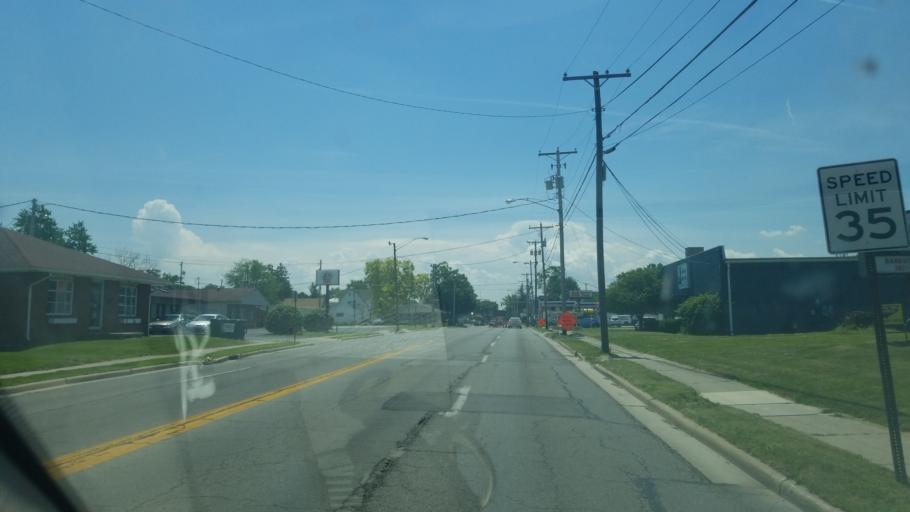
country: US
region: Ohio
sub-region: Hancock County
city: Findlay
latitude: 41.0386
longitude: -83.6413
